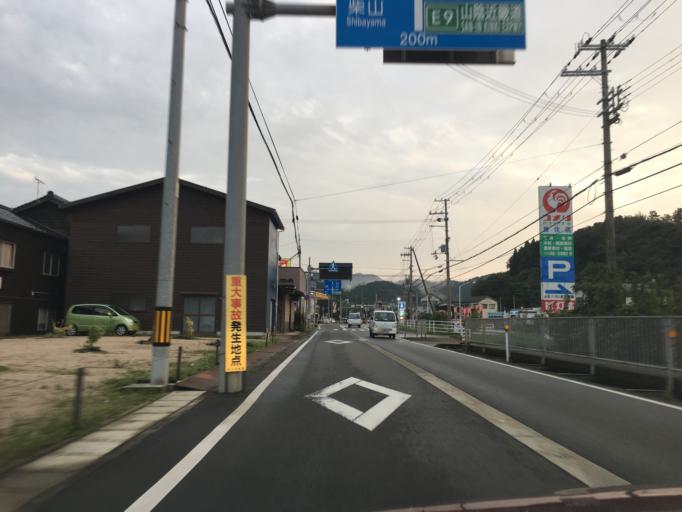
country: JP
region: Hyogo
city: Toyooka
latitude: 35.6331
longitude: 134.6267
